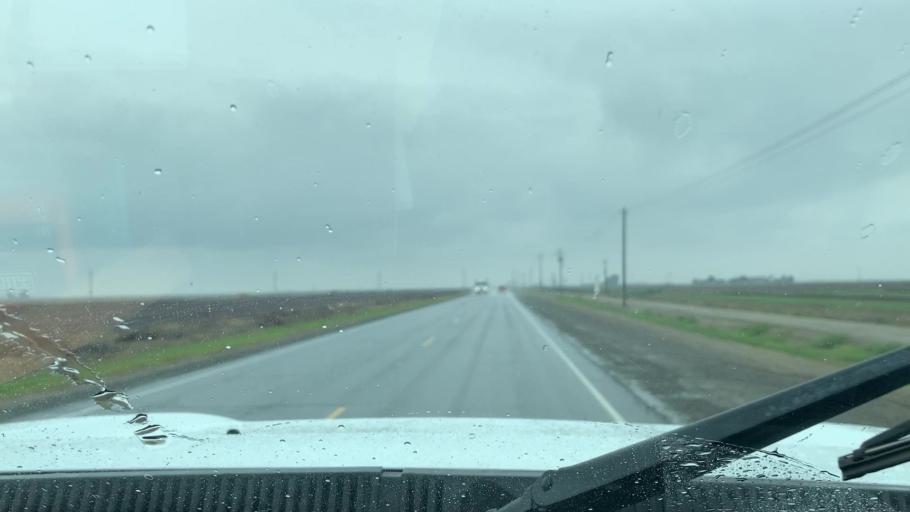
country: US
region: California
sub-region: Tulare County
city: Alpaugh
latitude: 35.9515
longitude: -119.4491
